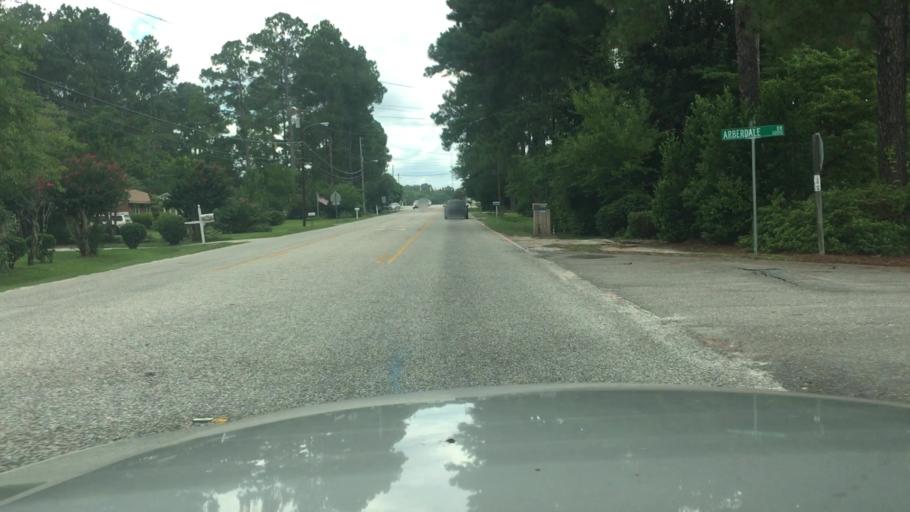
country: US
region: North Carolina
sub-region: Cumberland County
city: Hope Mills
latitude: 35.0405
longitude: -78.9851
